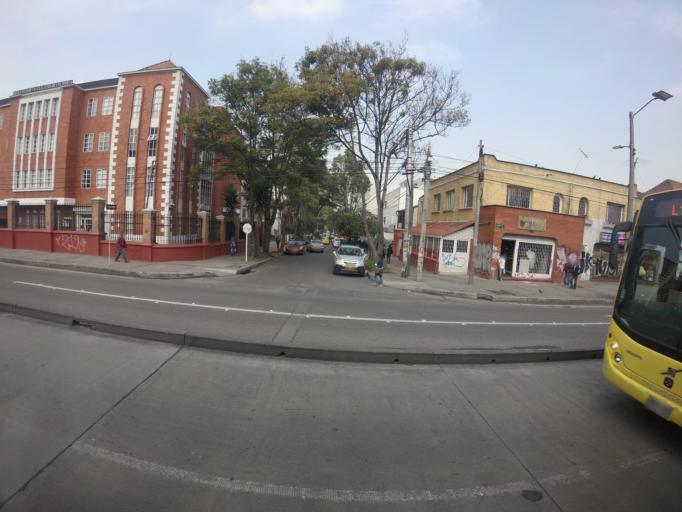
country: CO
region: Bogota D.C.
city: Bogota
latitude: 4.6269
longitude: -74.0688
